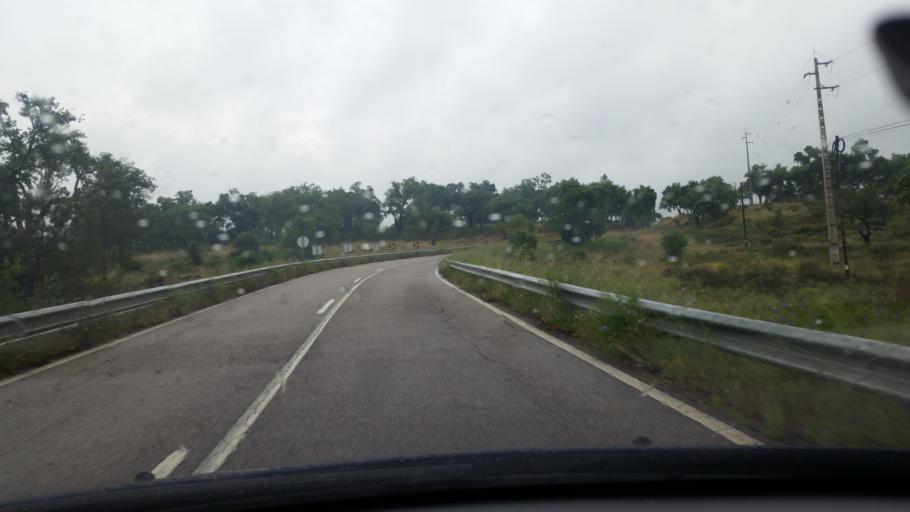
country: PT
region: Portalegre
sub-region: Avis
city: Avis
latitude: 39.1232
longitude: -7.9739
